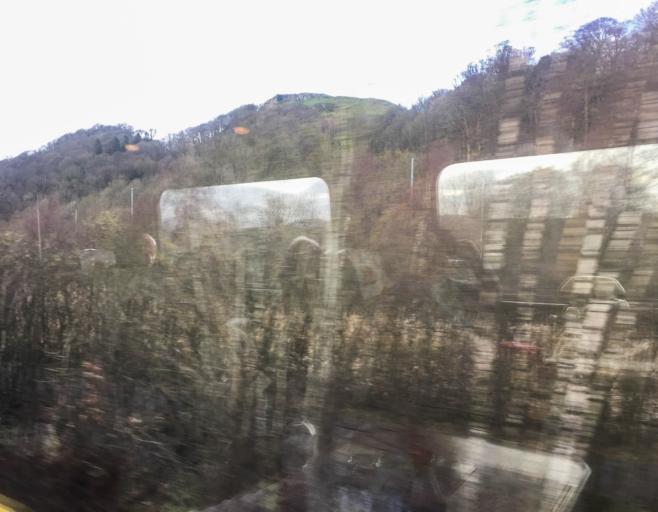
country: GB
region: Scotland
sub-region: Renfrewshire
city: Bishopton
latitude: 55.9323
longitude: -4.5077
